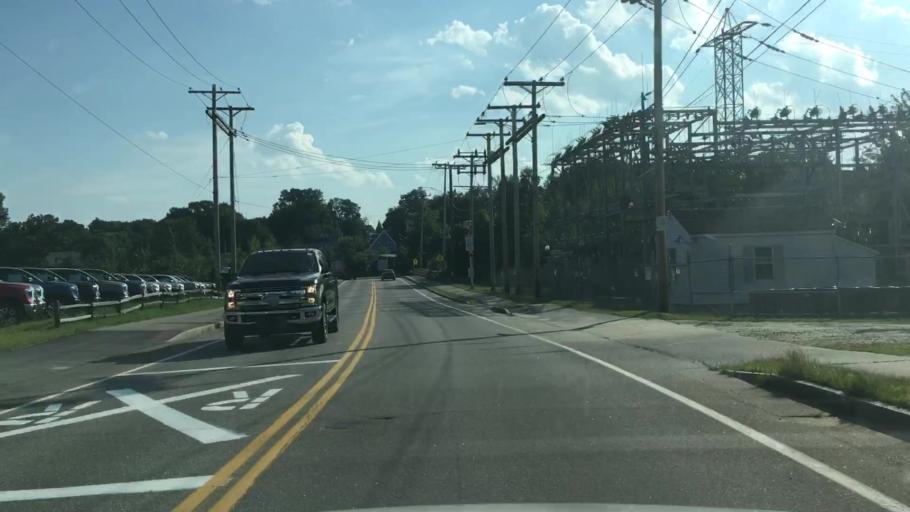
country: US
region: New Hampshire
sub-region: Belknap County
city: Laconia
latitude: 43.5366
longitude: -71.4678
